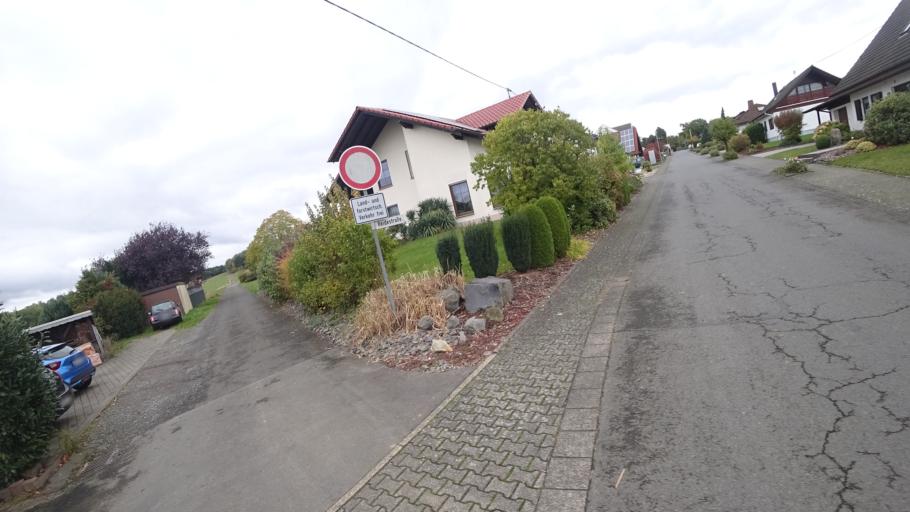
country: DE
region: Rheinland-Pfalz
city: Maxsain
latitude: 50.5457
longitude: 7.7821
